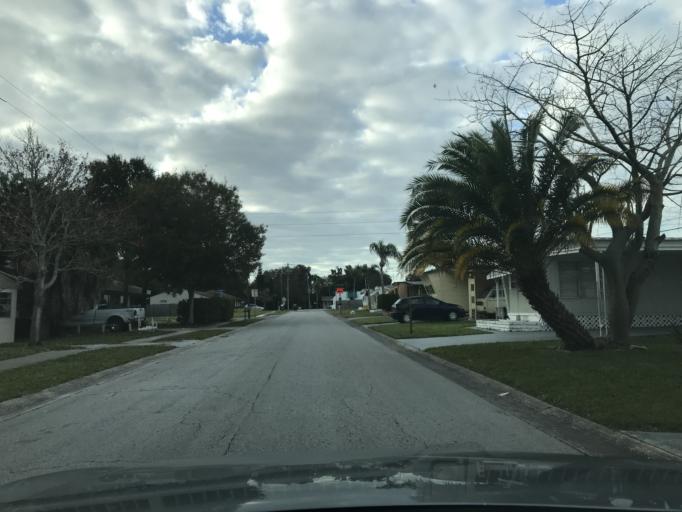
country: US
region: Florida
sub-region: Pinellas County
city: Clearwater
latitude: 27.9512
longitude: -82.7834
